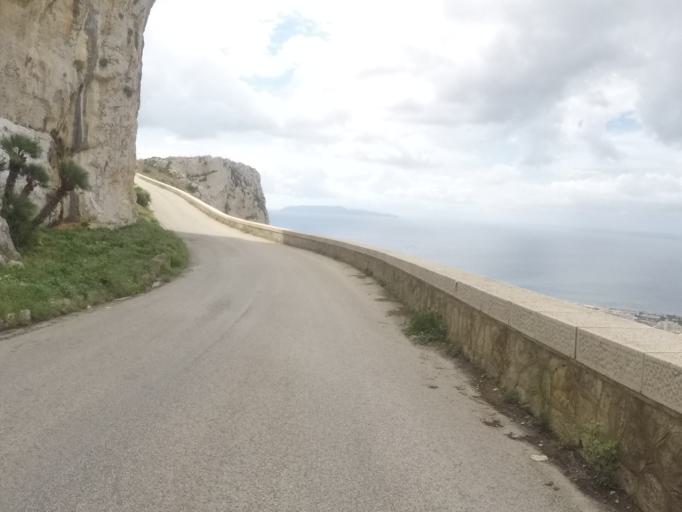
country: IT
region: Sicily
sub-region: Trapani
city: Casa Santa
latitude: 38.0369
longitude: 12.5571
